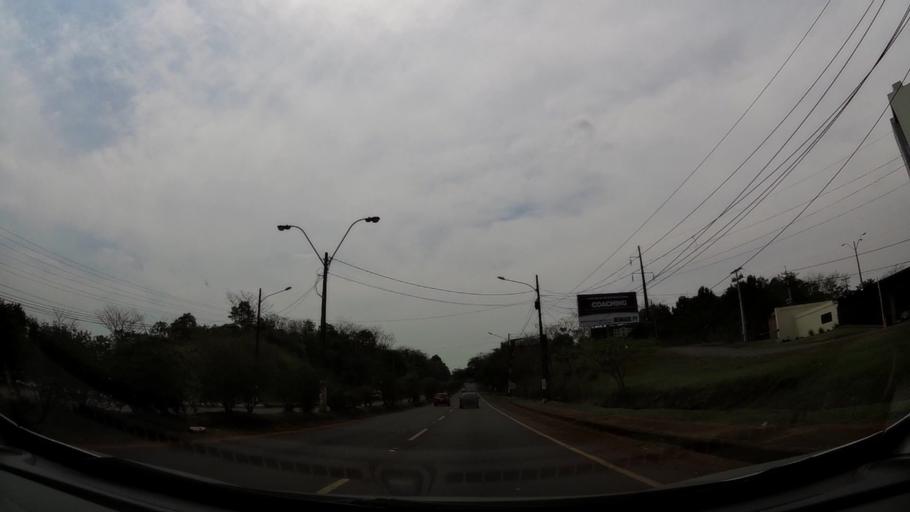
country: PY
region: Alto Parana
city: Ciudad del Este
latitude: -25.4894
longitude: -54.6303
